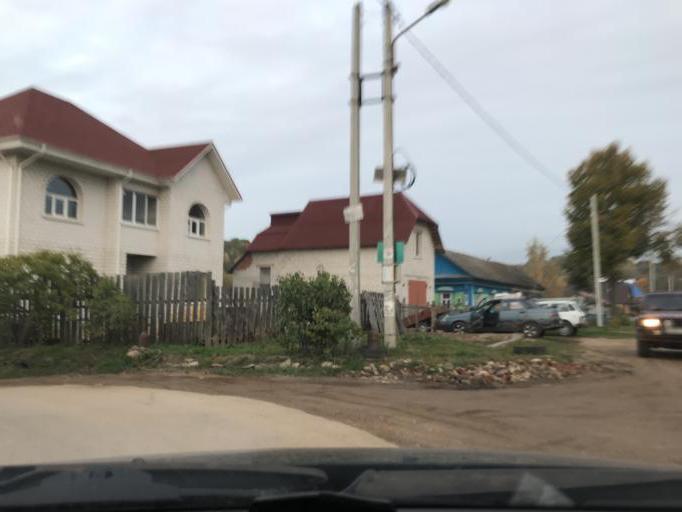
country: RU
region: Kaluga
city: Kaluga
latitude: 54.5495
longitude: 36.2246
